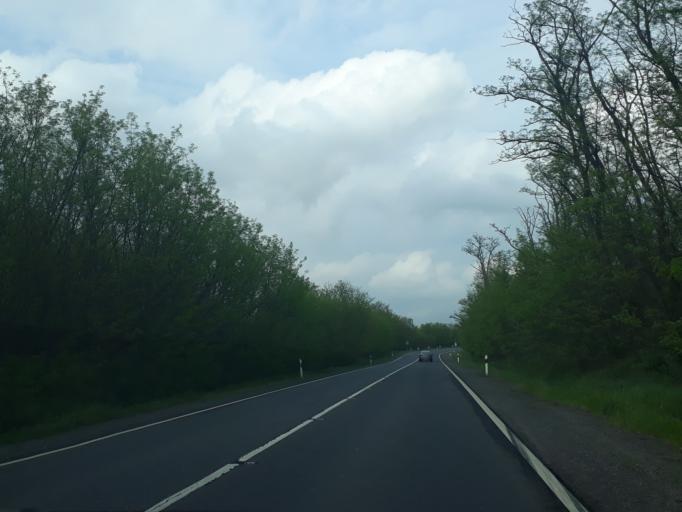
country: HU
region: Szabolcs-Szatmar-Bereg
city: Nyirtass
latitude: 48.1396
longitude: 22.0217
